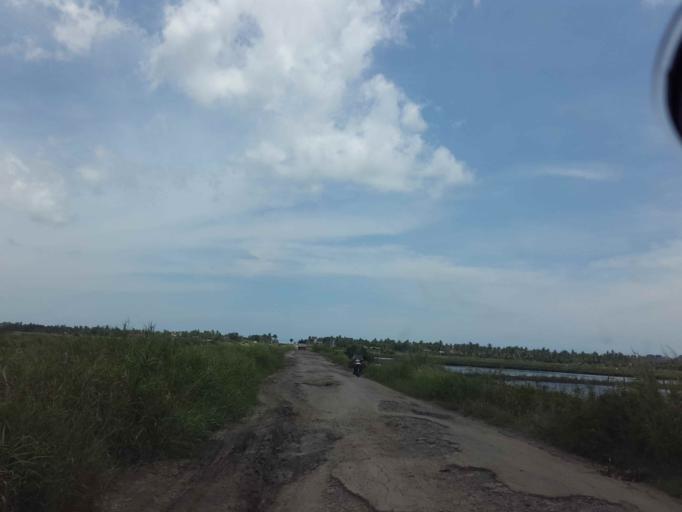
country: ID
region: Lampung
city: Palas
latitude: -5.6260
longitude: 105.7756
